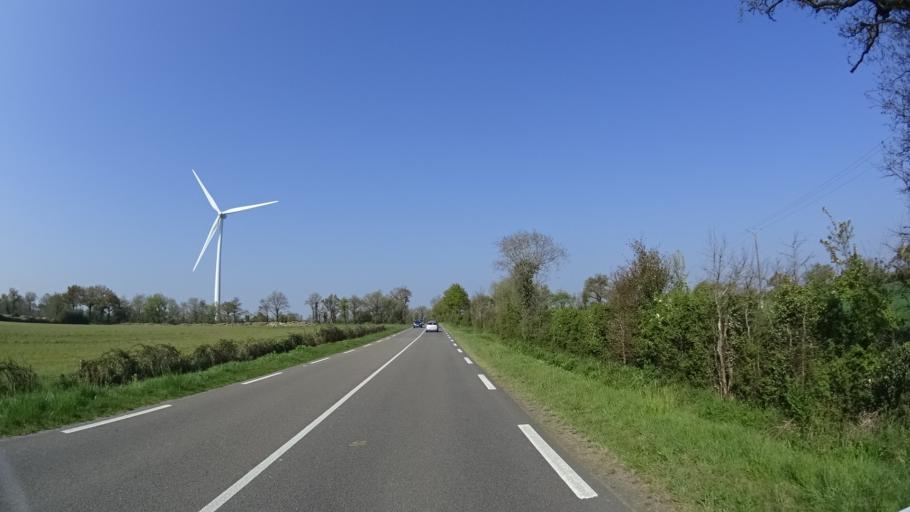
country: FR
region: Pays de la Loire
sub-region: Departement de la Loire-Atlantique
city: Saint-Hilaire-de-Chaleons
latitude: 47.0764
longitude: -1.8779
